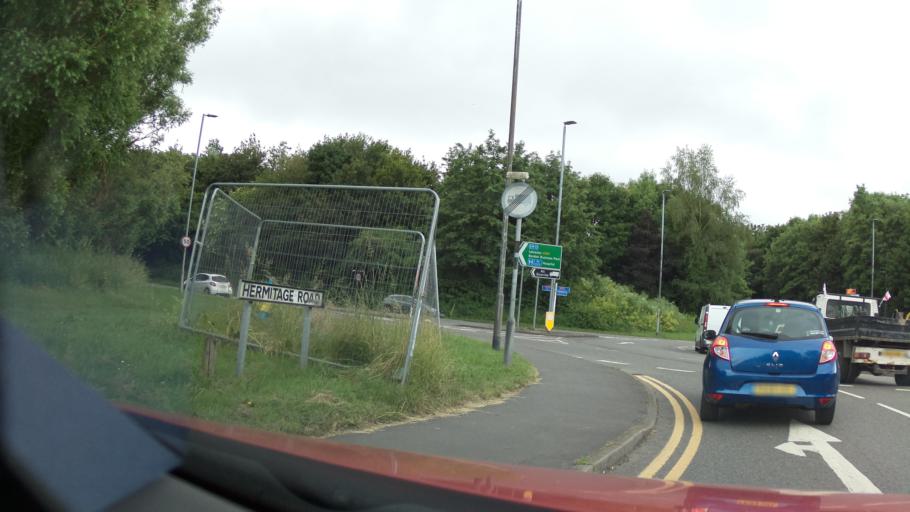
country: GB
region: England
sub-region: Leicestershire
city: Coalville
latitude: 52.7313
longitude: -1.3664
